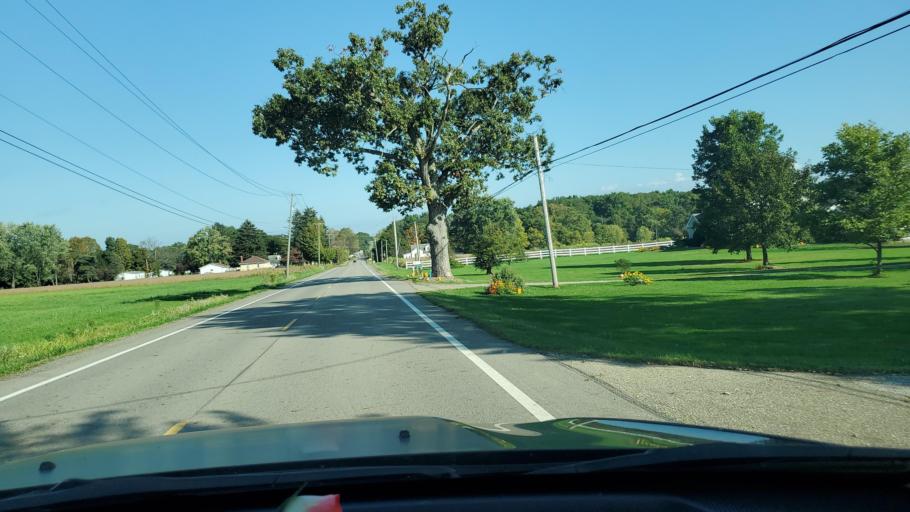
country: US
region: Ohio
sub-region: Trumbull County
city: Cortland
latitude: 41.4337
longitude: -80.5888
